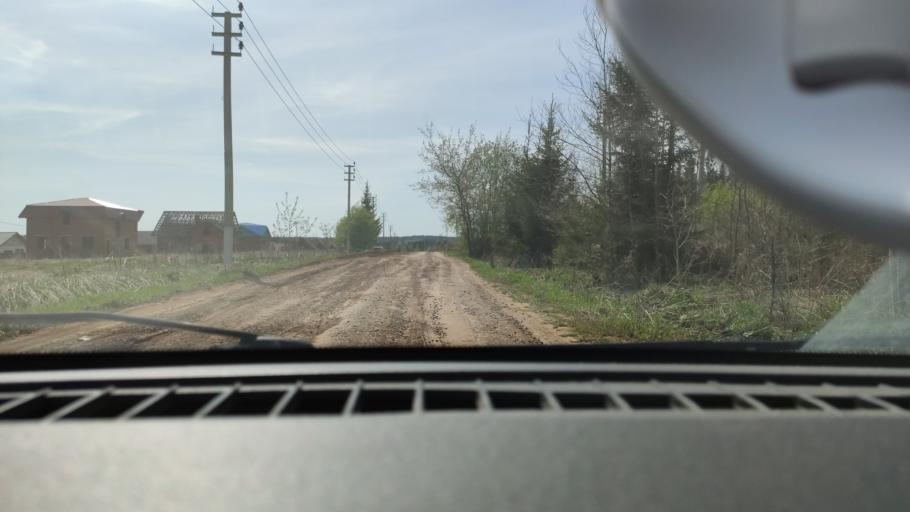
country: RU
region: Perm
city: Kultayevo
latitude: 57.8839
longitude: 55.8519
